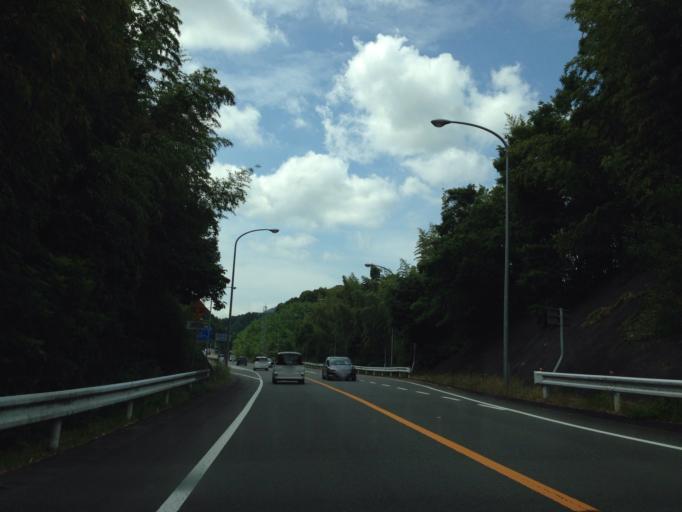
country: JP
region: Shizuoka
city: Mishima
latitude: 35.0455
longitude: 138.9209
